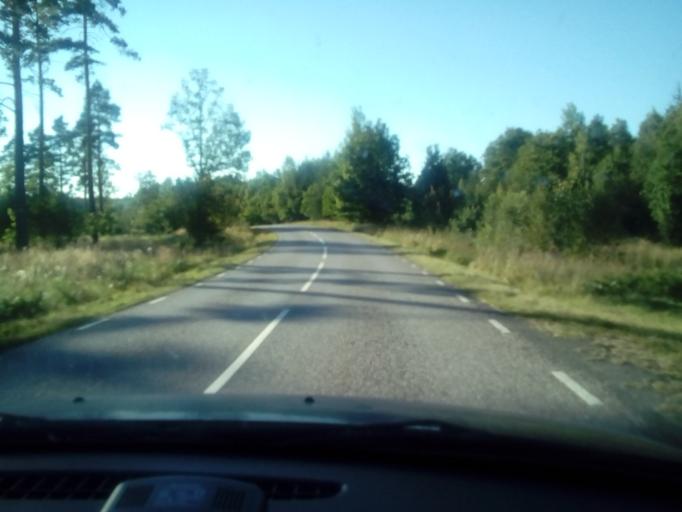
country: SE
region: Kalmar
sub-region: Vasterviks Kommun
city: Gamleby
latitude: 57.7926
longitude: 16.3787
